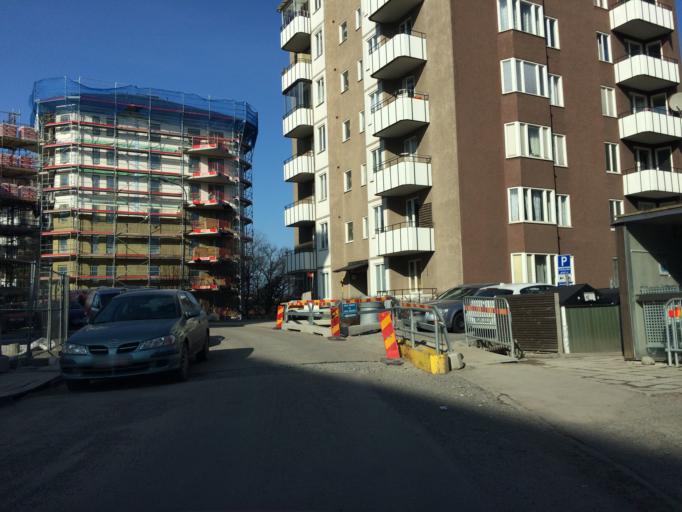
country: SE
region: Stockholm
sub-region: Stockholms Kommun
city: Arsta
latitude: 59.2892
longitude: 17.9986
